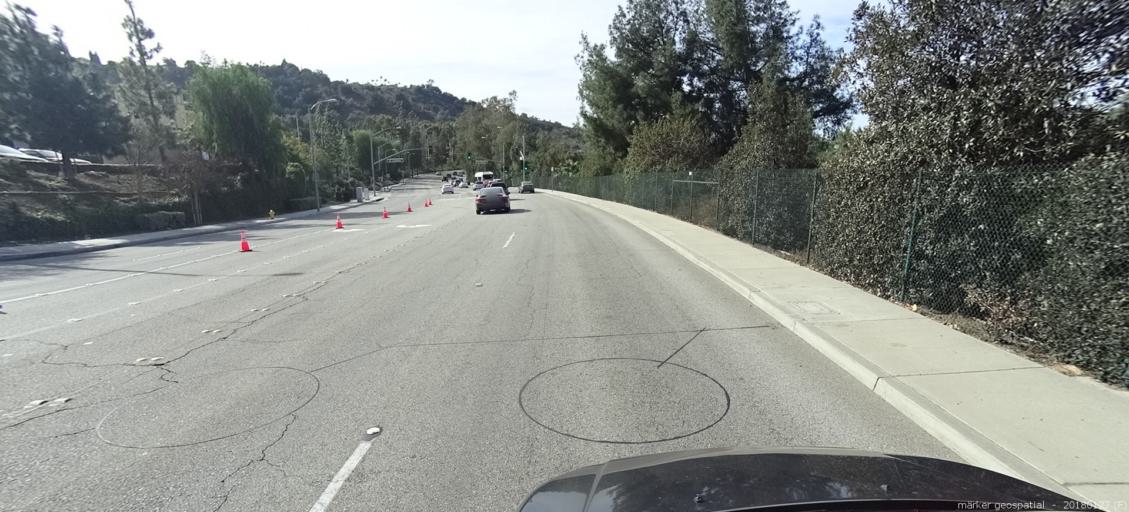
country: US
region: California
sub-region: Los Angeles County
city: Diamond Bar
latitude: 34.0061
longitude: -117.8228
